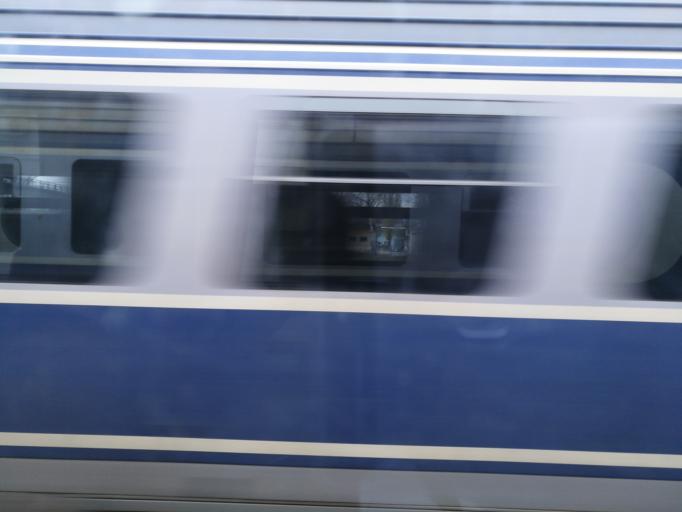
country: RO
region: Bacau
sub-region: Municipiul Bacau
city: Bacau
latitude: 46.5652
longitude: 26.8953
